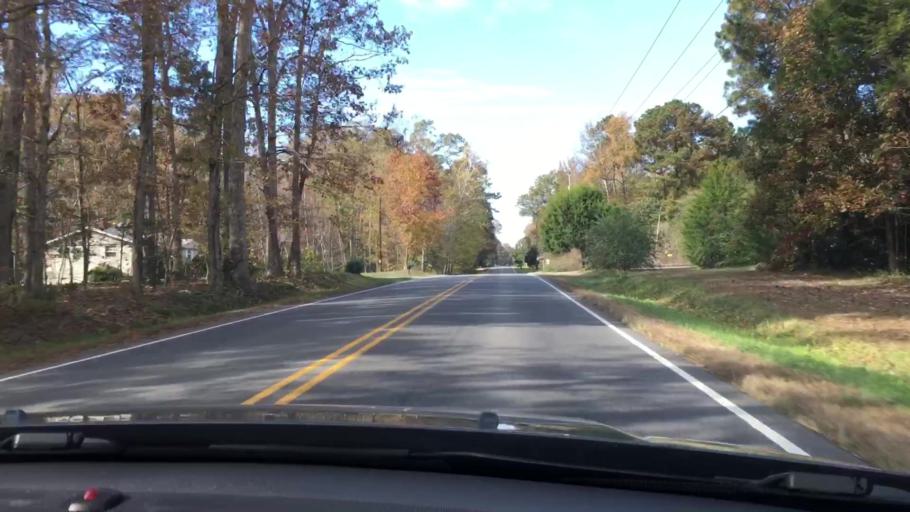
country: US
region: Virginia
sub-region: King William County
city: West Point
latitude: 37.5694
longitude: -76.8341
